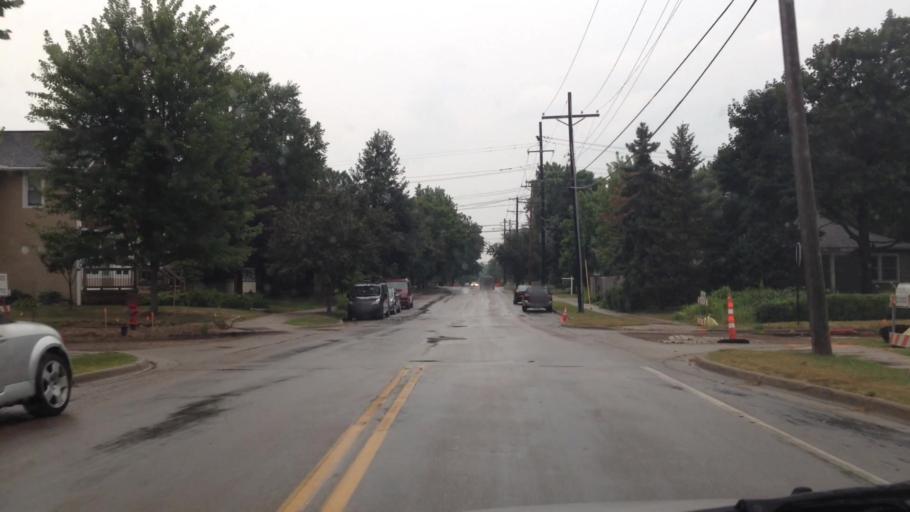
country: US
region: Minnesota
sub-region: Hennepin County
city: Saint Louis Park
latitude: 44.9359
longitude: -93.3562
